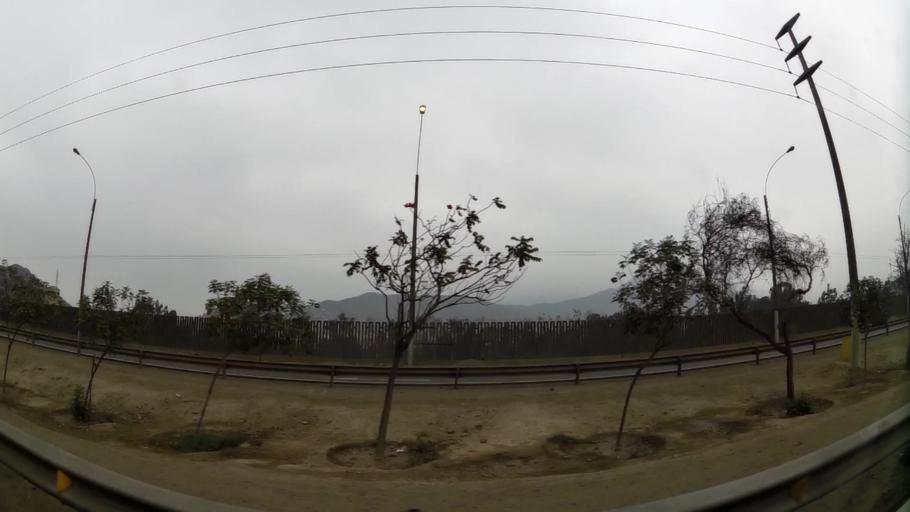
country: PE
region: Lima
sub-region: Lima
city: Vitarte
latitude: -12.0285
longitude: -76.9758
